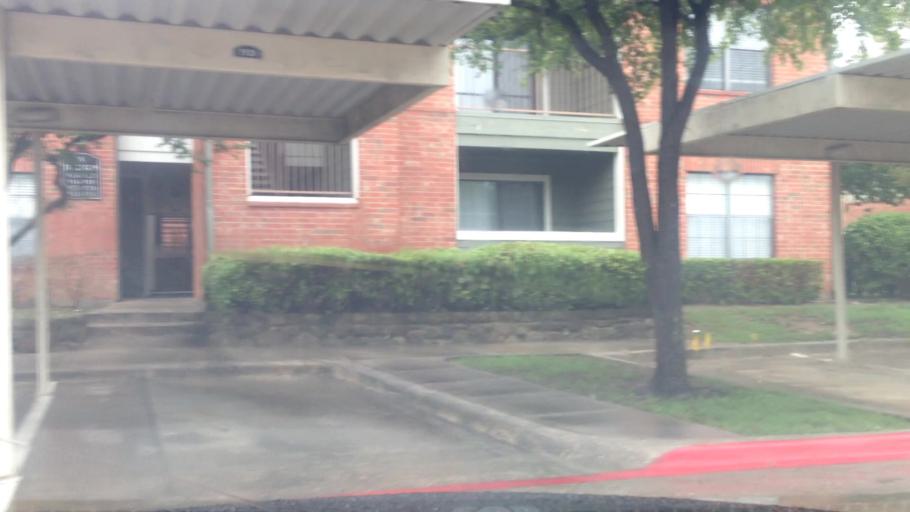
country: US
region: Texas
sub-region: Tarrant County
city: Watauga
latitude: 32.8774
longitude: -97.2341
